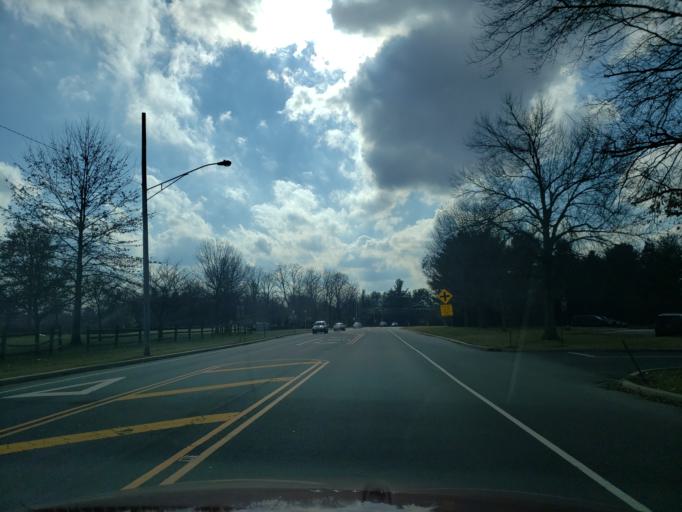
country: US
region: New Jersey
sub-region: Hunterdon County
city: Flemington
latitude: 40.5030
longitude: -74.8723
